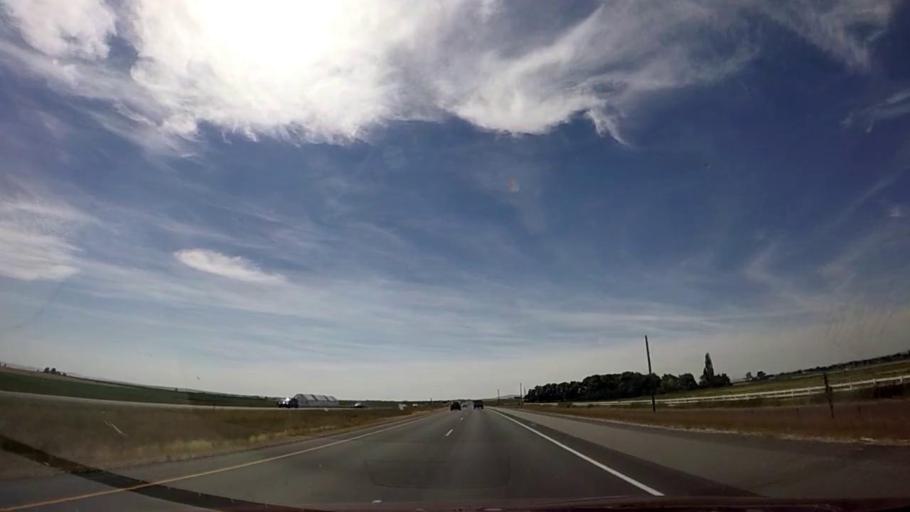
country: US
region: Idaho
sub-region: Twin Falls County
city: Hansen
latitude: 42.5763
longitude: -114.1161
